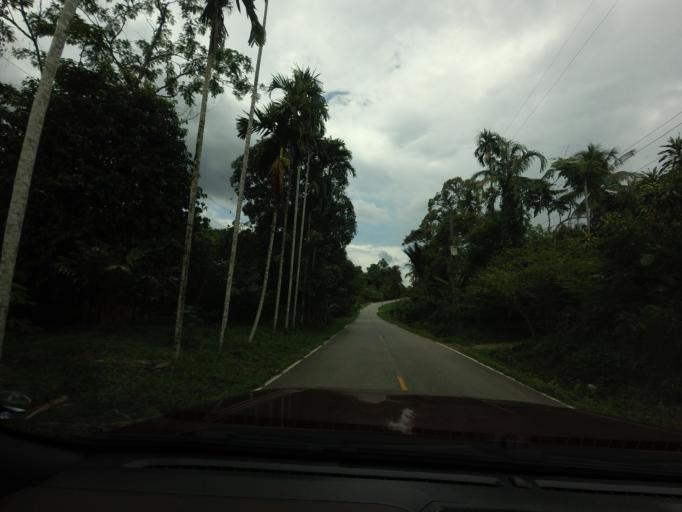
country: TH
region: Narathiwat
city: Sukhirin
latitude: 5.9850
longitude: 101.7058
